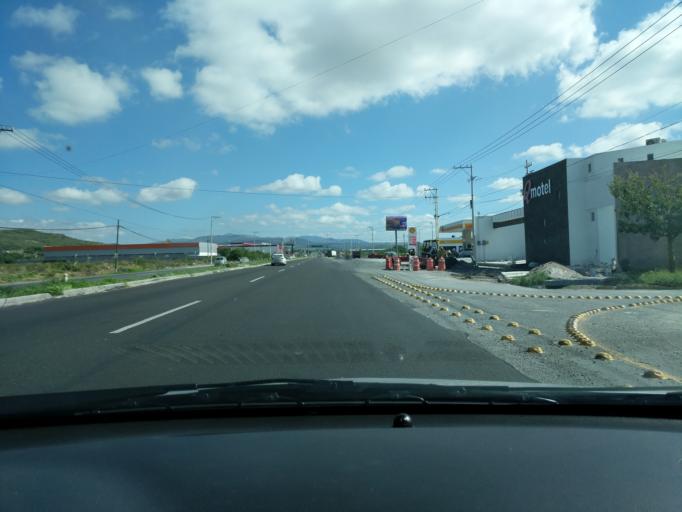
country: MX
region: Queretaro
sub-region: Queretaro
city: Patria Nueva
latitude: 20.6361
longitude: -100.4997
